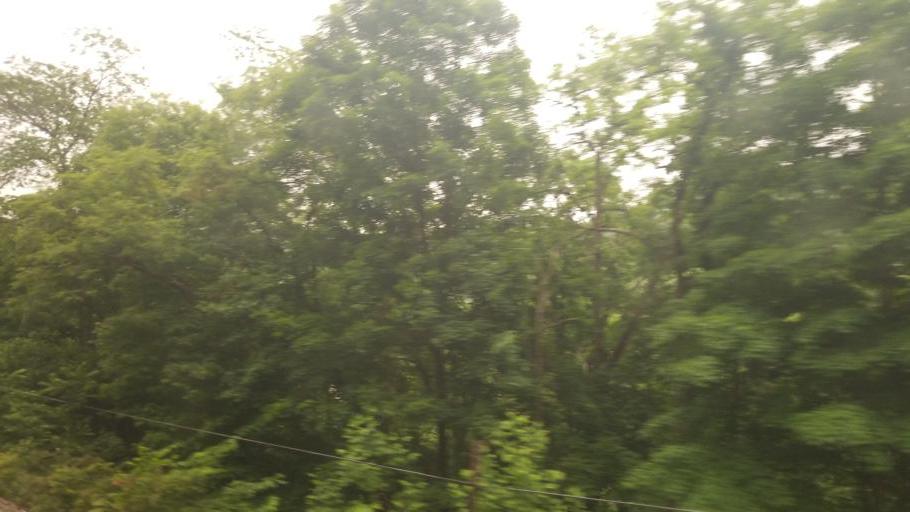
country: US
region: Pennsylvania
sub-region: Somerset County
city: Milford
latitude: 39.8346
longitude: -79.2657
